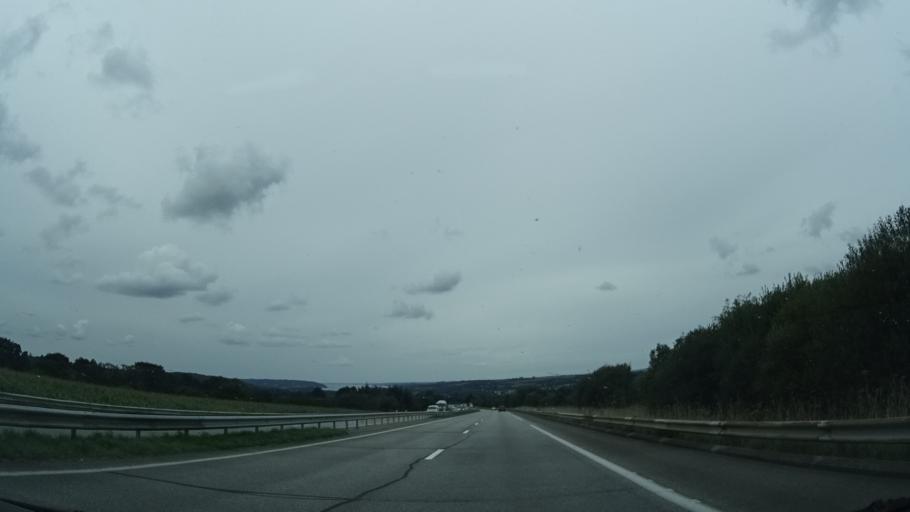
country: FR
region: Brittany
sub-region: Departement du Finistere
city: Le Faou
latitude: 48.2850
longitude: -4.1482
